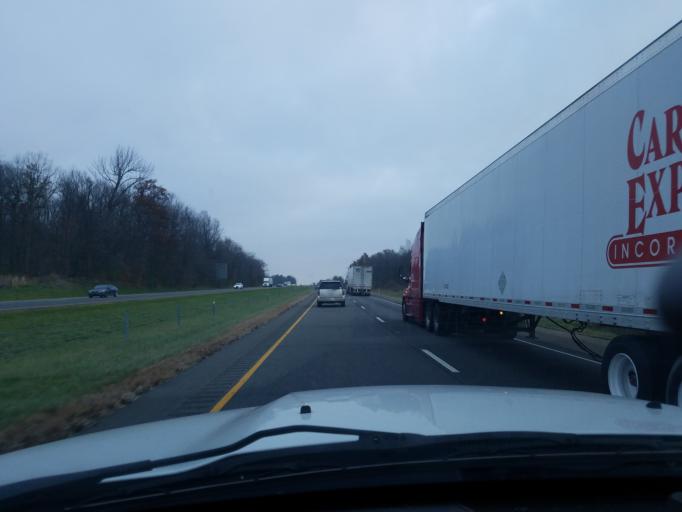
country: US
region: Indiana
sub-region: Delaware County
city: Daleville
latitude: 40.1449
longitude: -85.5670
